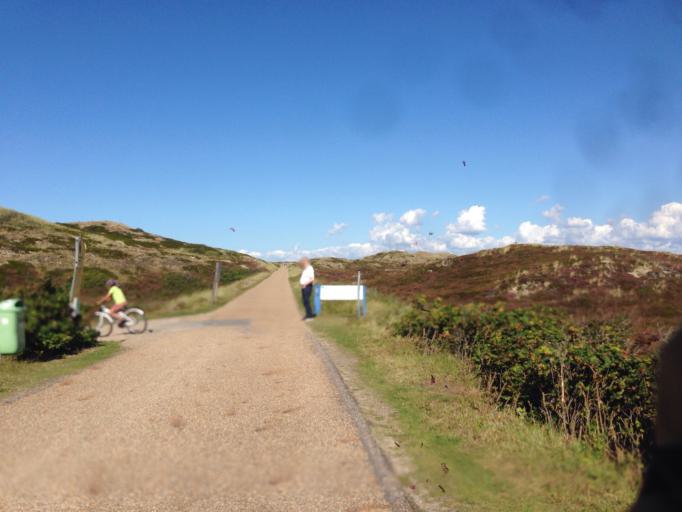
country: DE
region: Schleswig-Holstein
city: Tinnum
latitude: 54.9653
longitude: 8.3414
